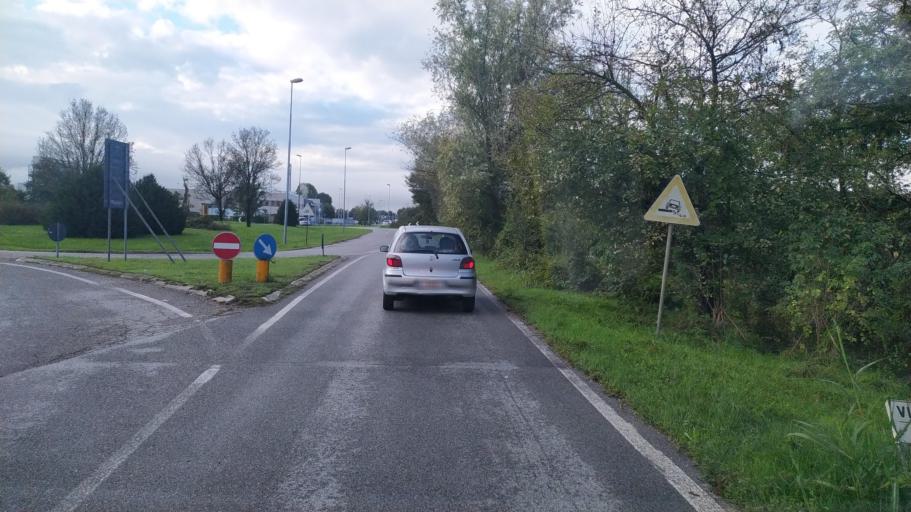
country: IT
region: Lombardy
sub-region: Citta metropolitana di Milano
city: Gaggiano
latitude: 45.3907
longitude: 9.0285
